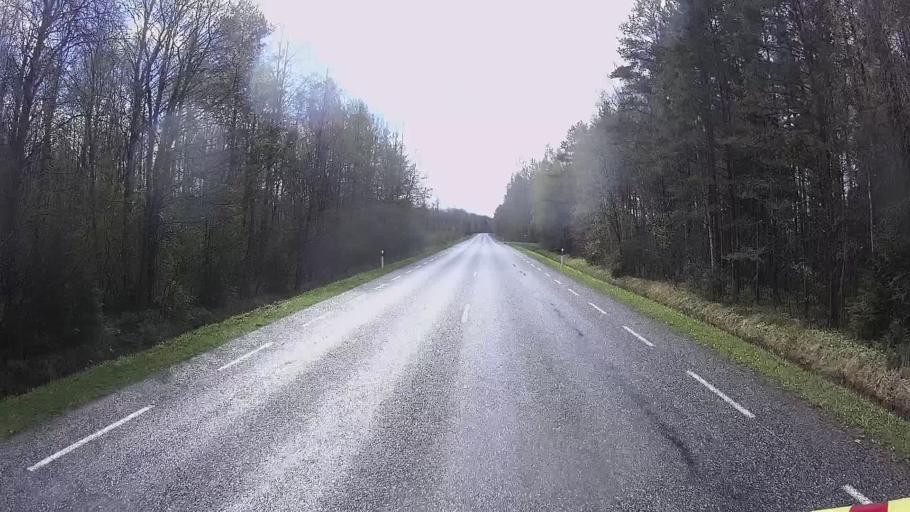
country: EE
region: Hiiumaa
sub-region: Kaerdla linn
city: Kardla
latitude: 58.9041
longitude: 22.9298
